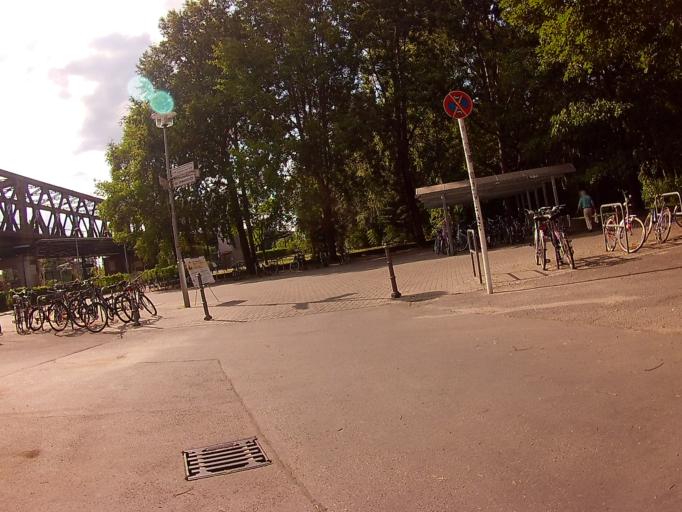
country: DE
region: Berlin
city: Rummelsburg
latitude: 52.4935
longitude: 13.4995
